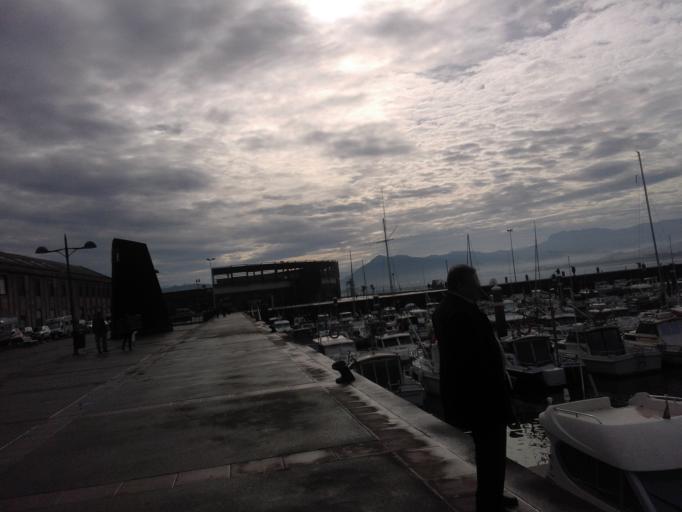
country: ES
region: Cantabria
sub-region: Provincia de Cantabria
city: Santona
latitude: 43.4410
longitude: -3.4613
